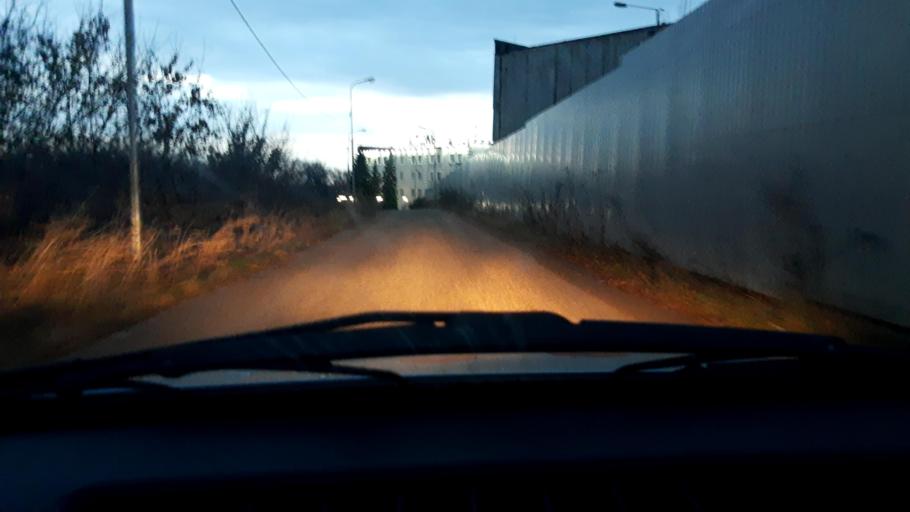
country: RU
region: Bashkortostan
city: Avdon
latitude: 54.6748
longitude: 55.8057
